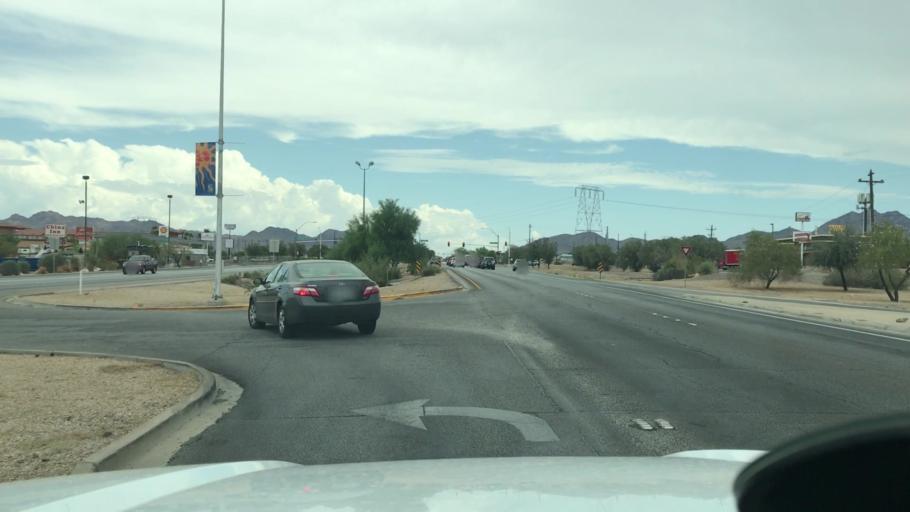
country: US
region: Nevada
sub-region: Clark County
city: Henderson
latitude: 36.0260
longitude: -114.9669
